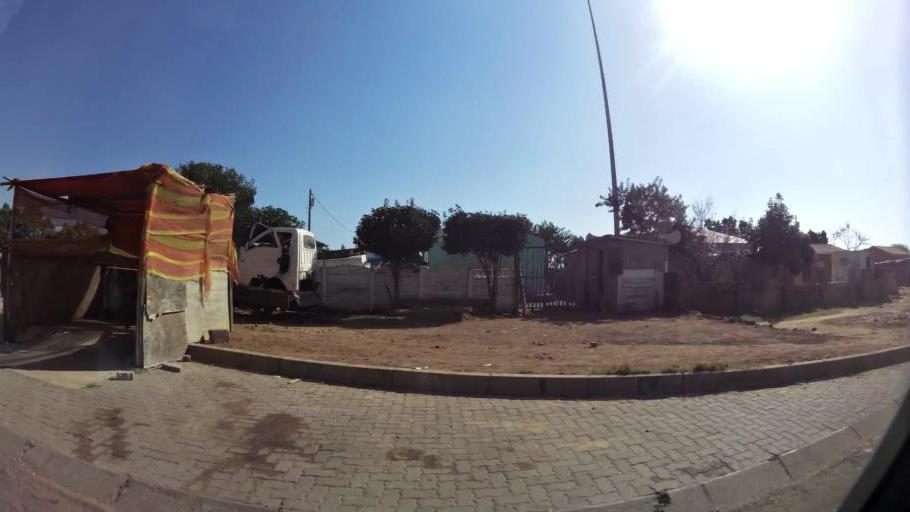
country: ZA
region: Gauteng
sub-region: City of Tshwane Metropolitan Municipality
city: Mabopane
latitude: -25.5544
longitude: 28.1014
